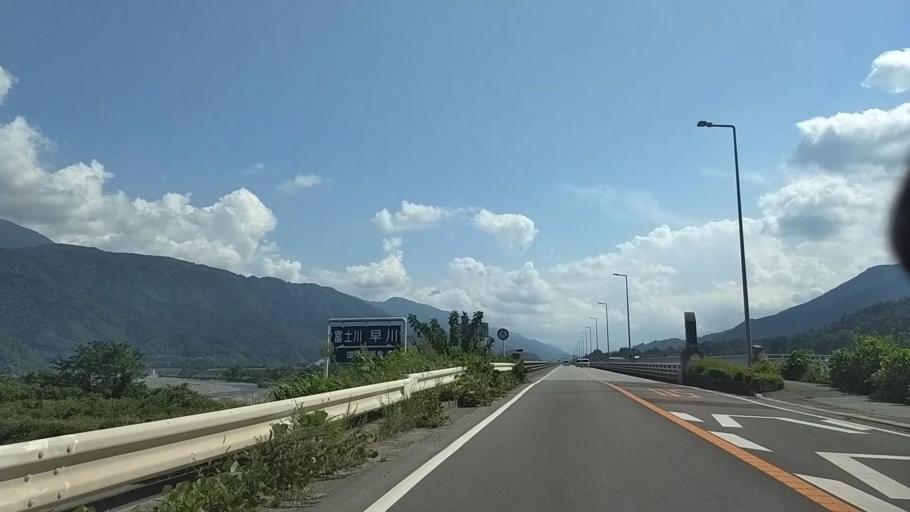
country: JP
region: Yamanashi
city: Ryuo
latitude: 35.4310
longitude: 138.4435
